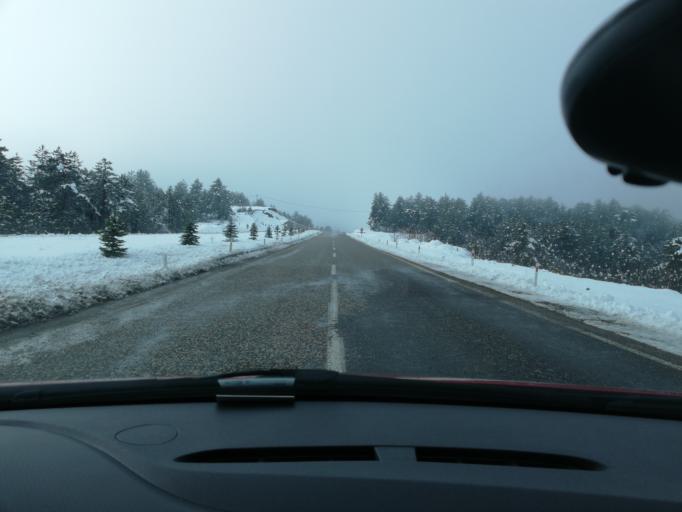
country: TR
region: Kastamonu
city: Akkaya
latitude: 41.2869
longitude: 33.4715
